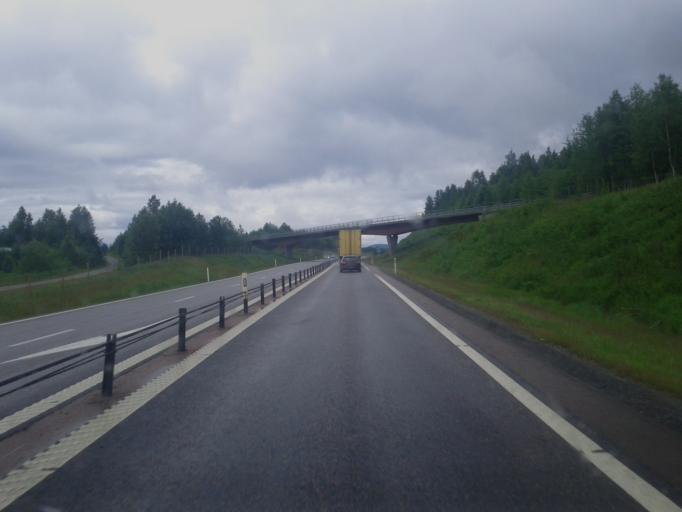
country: SE
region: Vaesternorrland
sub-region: Haernoesands Kommun
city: Haernoesand
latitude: 62.7600
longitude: 17.9048
